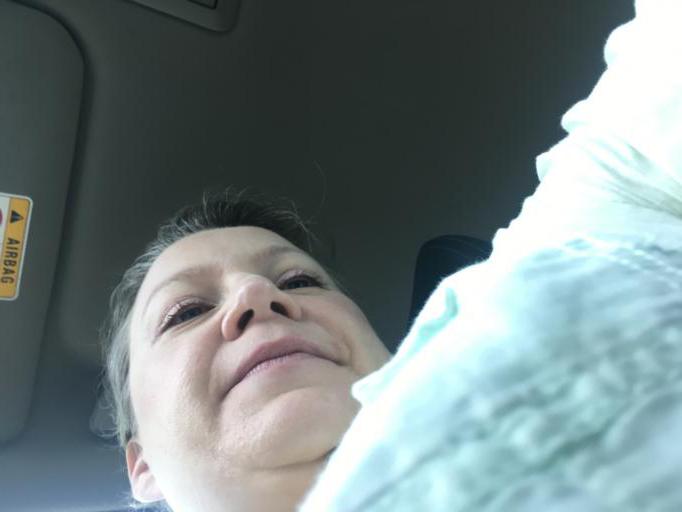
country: TH
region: Nong Khai
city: Si Chiang Mai
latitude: 17.9760
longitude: 102.5439
